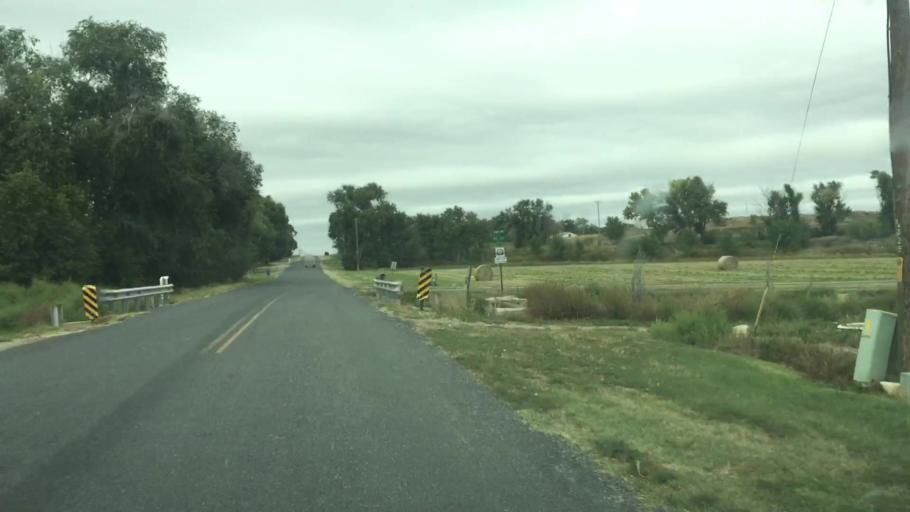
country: US
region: Kansas
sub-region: Hamilton County
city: Syracuse
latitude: 38.0570
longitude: -102.1186
